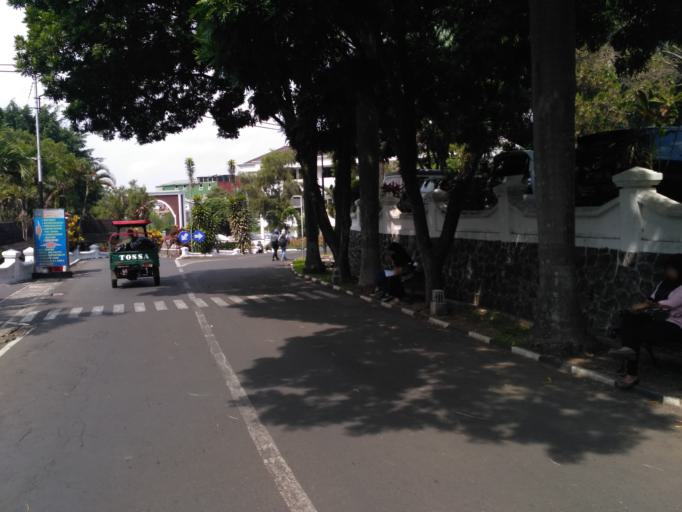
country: ID
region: East Java
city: Malang
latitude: -7.9210
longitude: 112.5978
